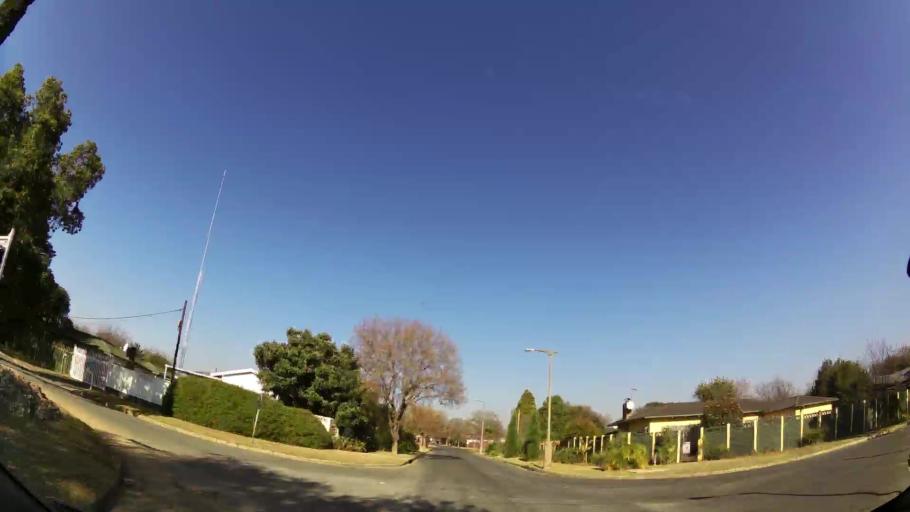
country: ZA
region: Gauteng
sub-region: Ekurhuleni Metropolitan Municipality
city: Benoni
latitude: -26.1548
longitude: 28.3133
